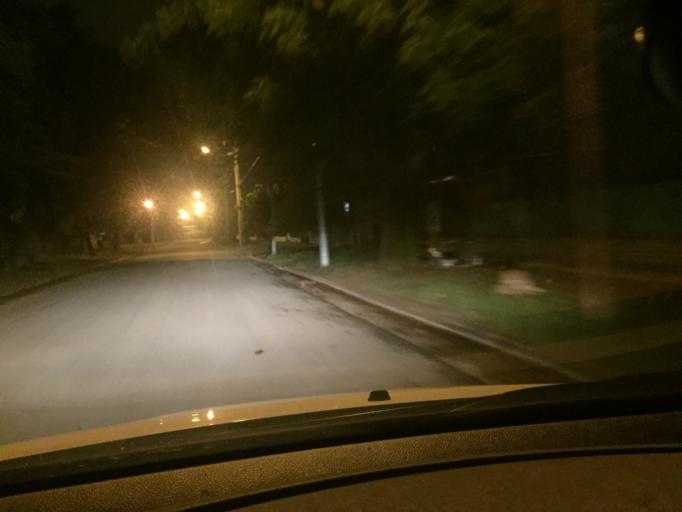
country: AR
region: Cordoba
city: Villa Allende
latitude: -31.3056
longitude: -64.2834
